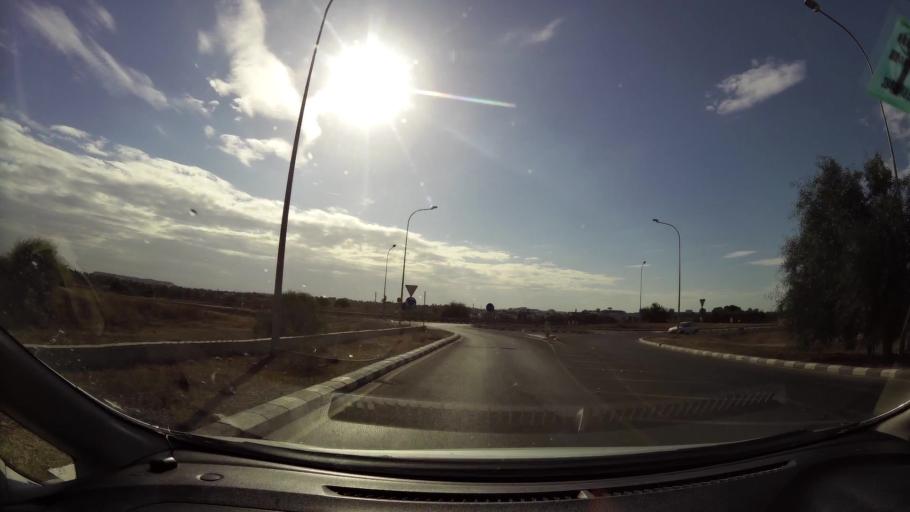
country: CY
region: Lefkosia
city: Nicosia
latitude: 35.1362
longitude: 33.3696
